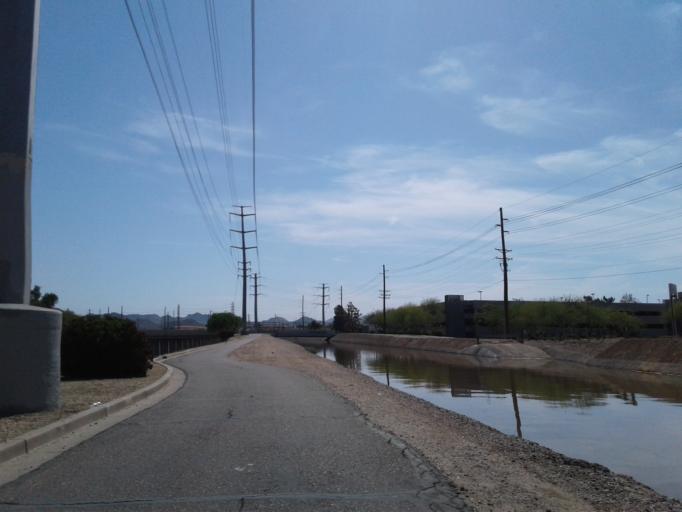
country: US
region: Arizona
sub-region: Maricopa County
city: Glendale
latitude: 33.5715
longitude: -112.1148
